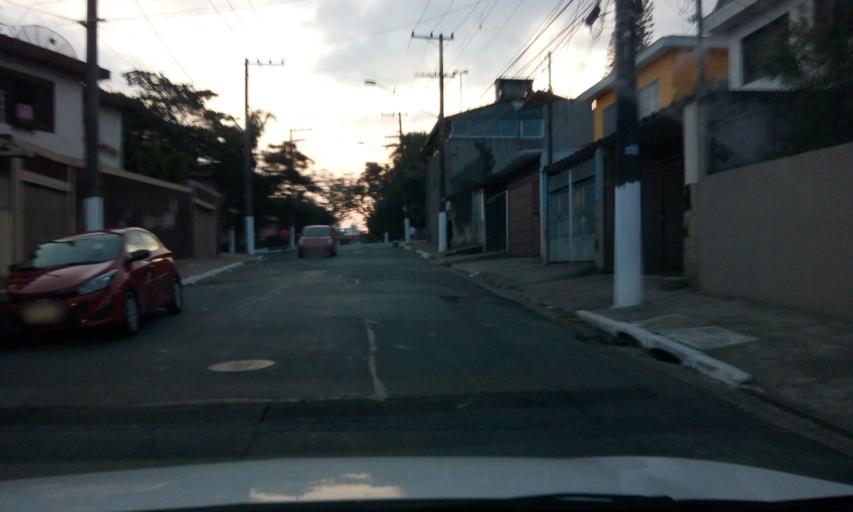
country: BR
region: Sao Paulo
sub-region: Diadema
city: Diadema
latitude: -23.6409
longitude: -46.6573
